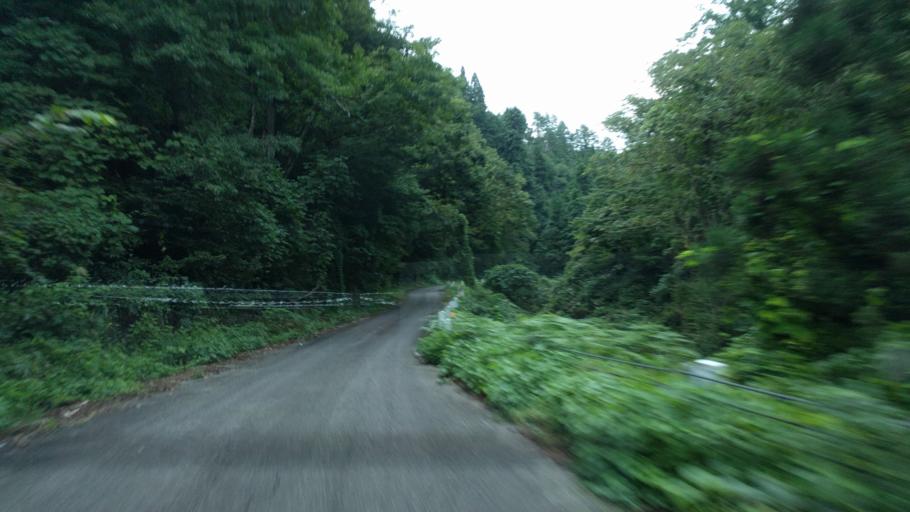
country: JP
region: Fukushima
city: Kitakata
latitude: 37.4661
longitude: 139.7953
